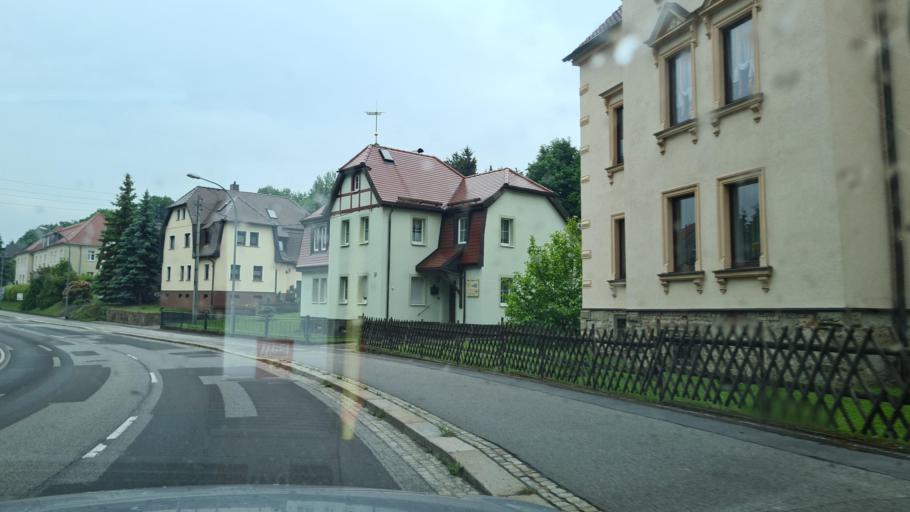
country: DE
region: Saxony
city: Kirschau
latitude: 51.0860
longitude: 14.4253
